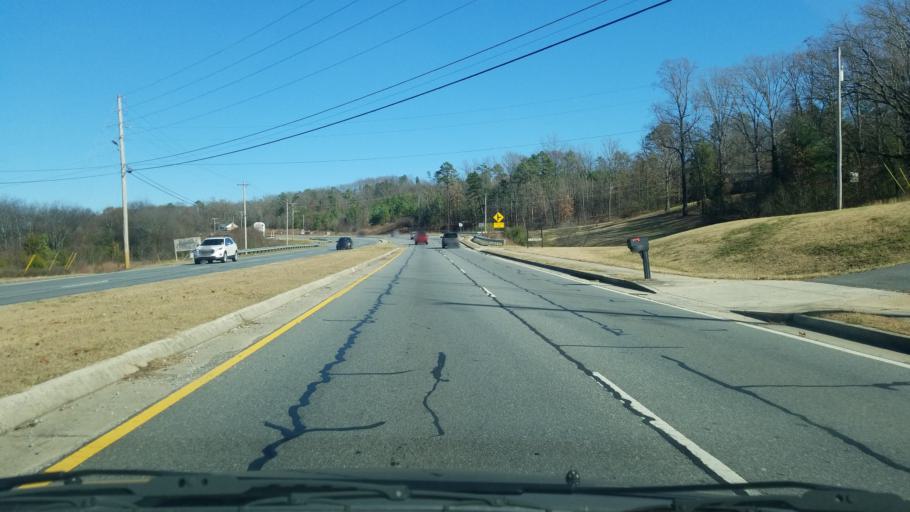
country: US
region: Georgia
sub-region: Catoosa County
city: Indian Springs
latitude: 34.9585
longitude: -85.1986
